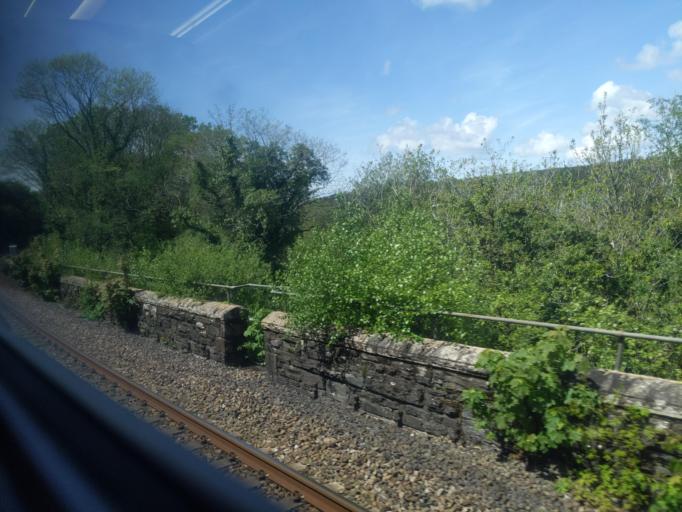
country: GB
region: England
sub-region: Cornwall
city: Liskeard
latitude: 50.4527
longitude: -4.5598
